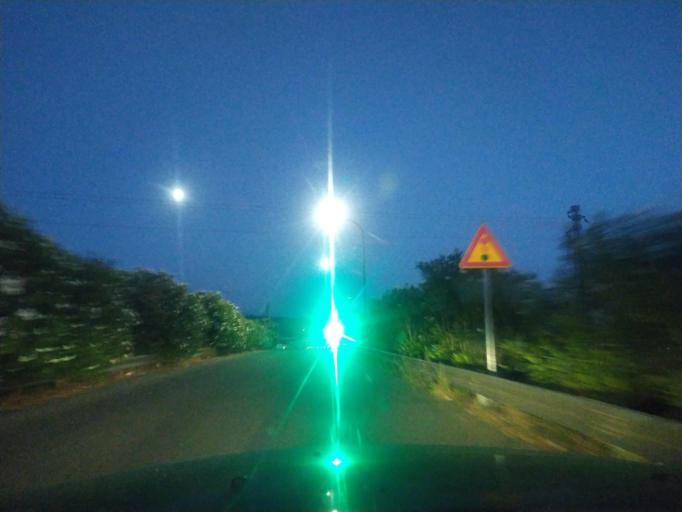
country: IT
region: Sicily
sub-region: Messina
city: Terme
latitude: 38.1427
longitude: 15.1599
